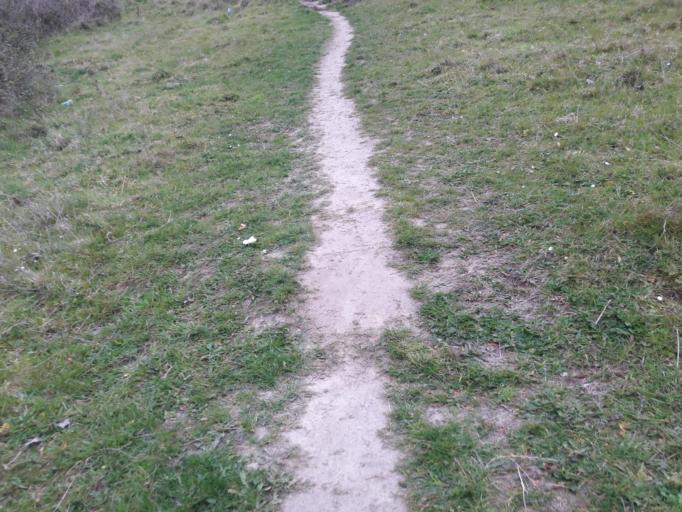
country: TR
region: Sinop
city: Sinop
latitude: 42.0217
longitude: 35.1256
